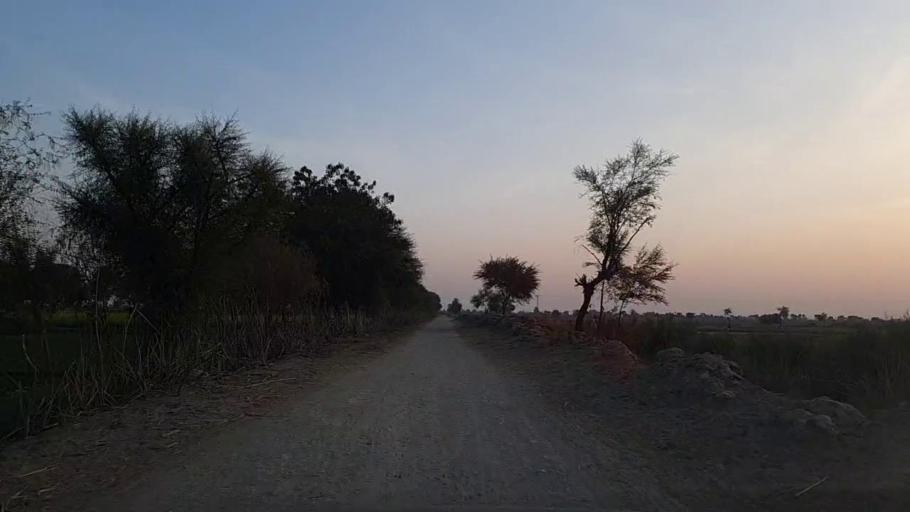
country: PK
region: Sindh
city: Tando Mittha Khan
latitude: 25.9540
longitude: 69.1164
